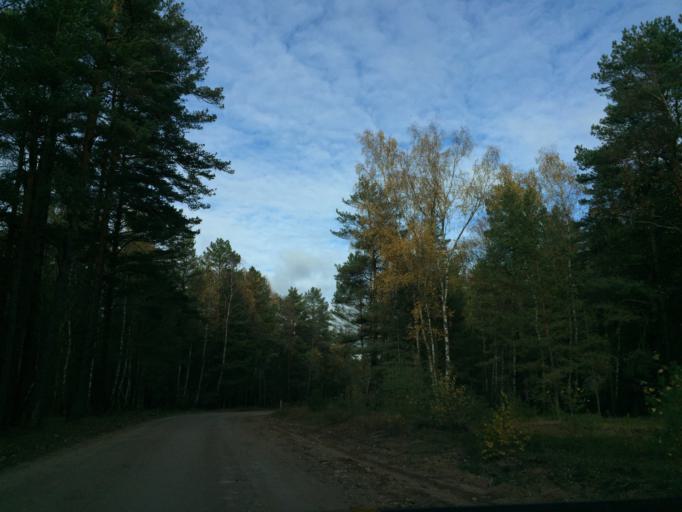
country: LV
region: Carnikava
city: Carnikava
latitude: 57.1402
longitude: 24.2654
